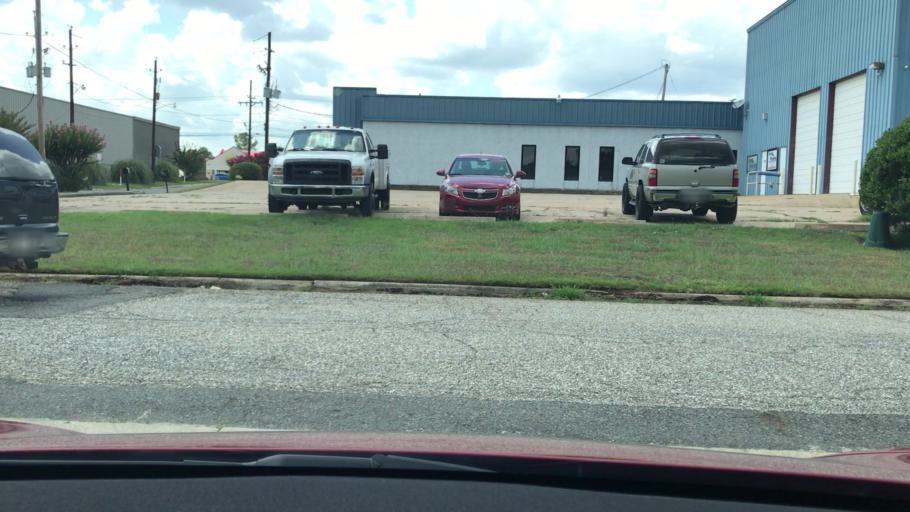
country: US
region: Louisiana
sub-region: De Soto Parish
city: Stonewall
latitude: 32.3989
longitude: -93.8055
